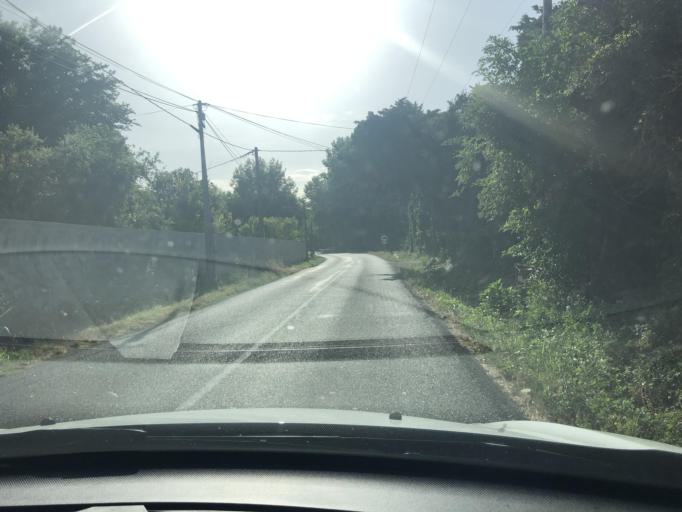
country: FR
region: Provence-Alpes-Cote d'Azur
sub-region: Departement du Vaucluse
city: Velleron
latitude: 43.9656
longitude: 4.9949
